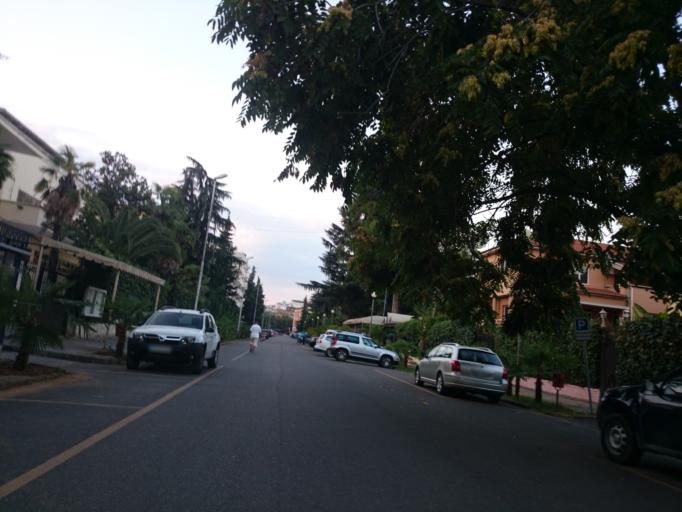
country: AL
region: Tirane
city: Tirana
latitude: 41.3302
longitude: 19.8079
